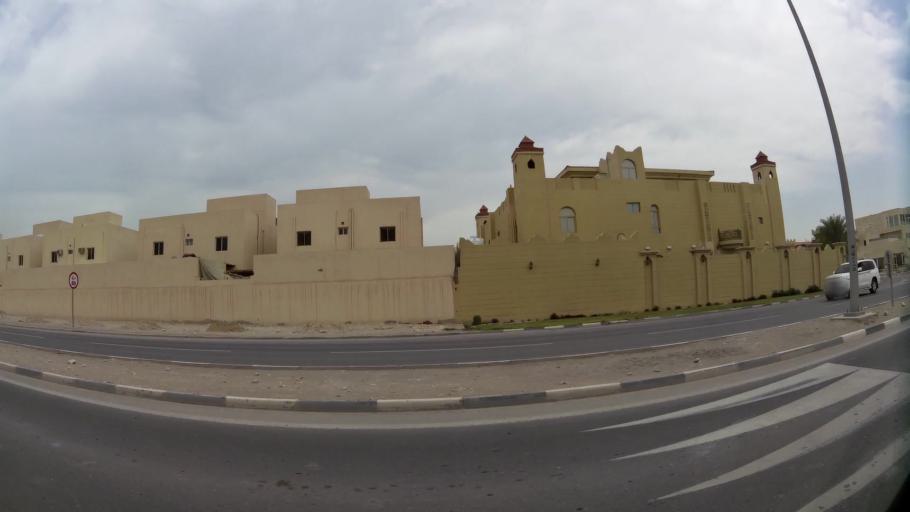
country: QA
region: Baladiyat ad Dawhah
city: Doha
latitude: 25.2220
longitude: 51.4690
